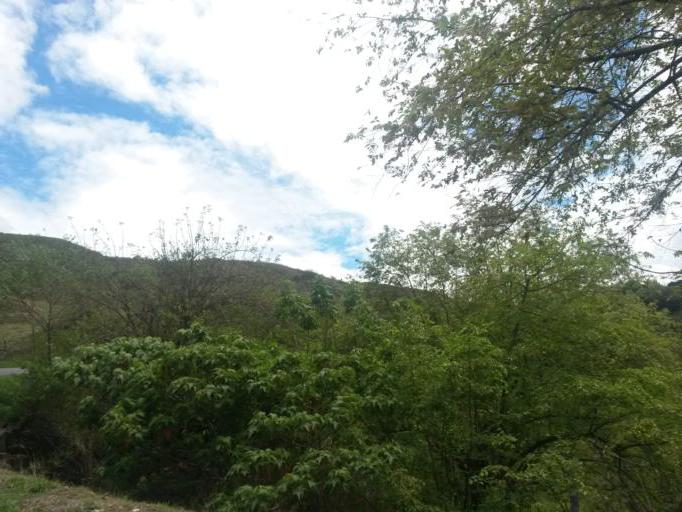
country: CO
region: Cauca
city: El Bordo
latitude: 2.0911
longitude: -76.9984
